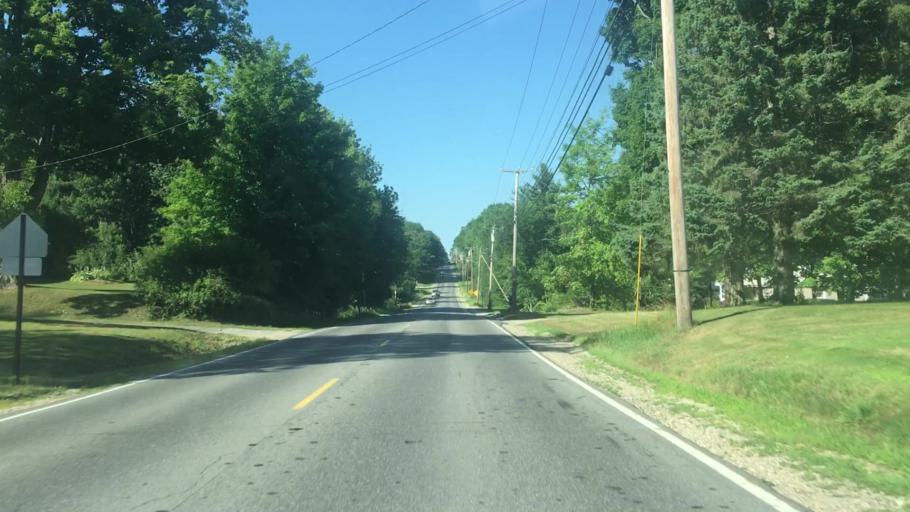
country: US
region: Maine
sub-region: York County
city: Buxton
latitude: 43.7392
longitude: -70.5473
